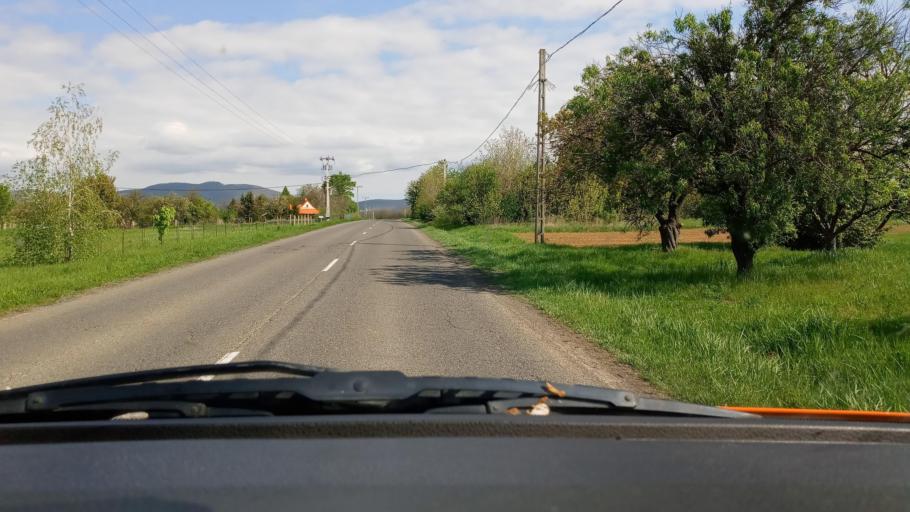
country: HU
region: Baranya
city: Hosszuheteny
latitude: 46.1171
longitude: 18.3478
